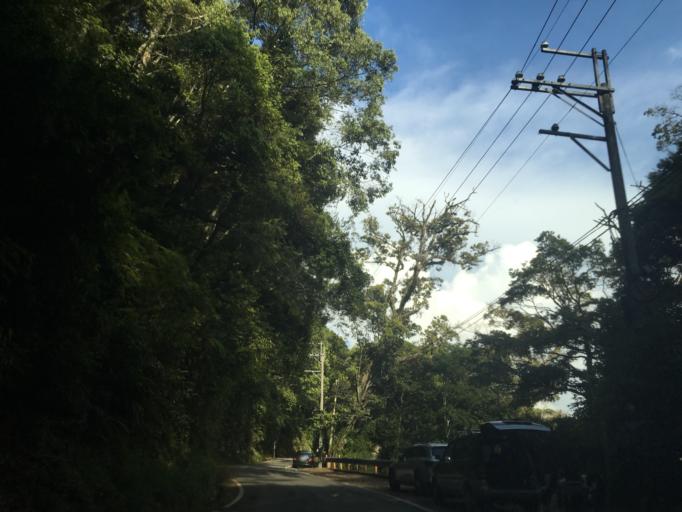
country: TW
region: Taiwan
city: Fengyuan
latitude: 24.2271
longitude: 120.9740
